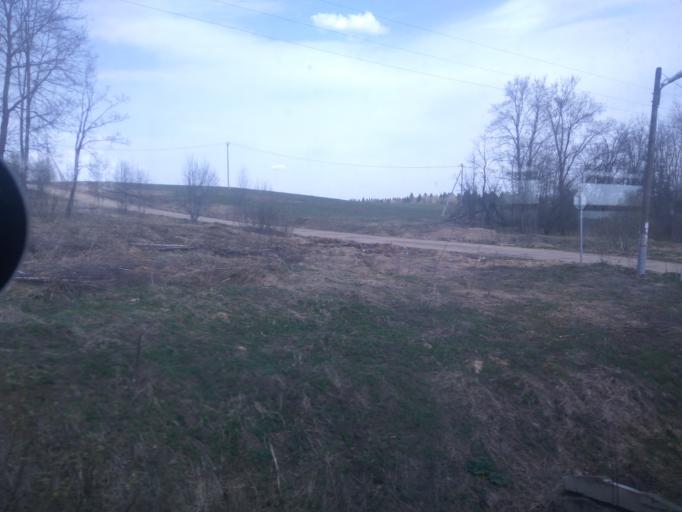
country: RU
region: Moskovskaya
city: Budenovetc
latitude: 56.3110
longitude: 37.6614
